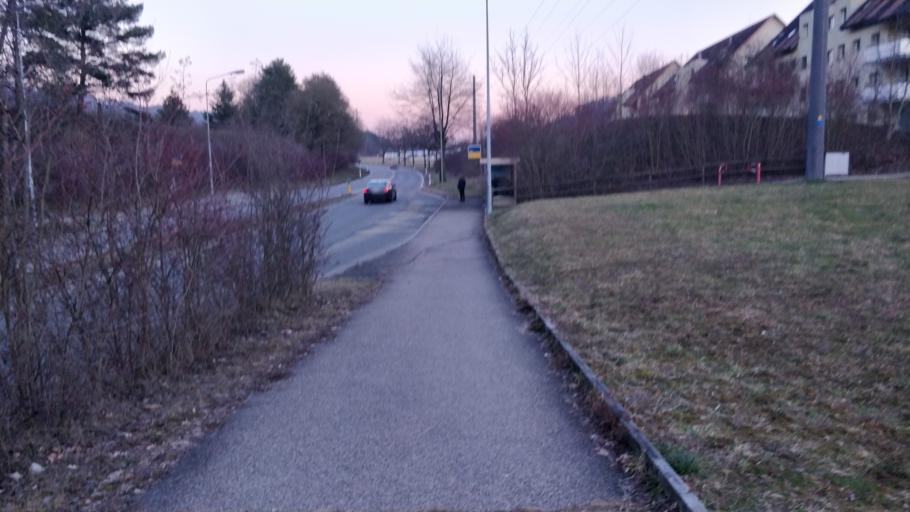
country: CH
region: Zurich
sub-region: Bezirk Buelach
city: Freienstein
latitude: 47.5226
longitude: 8.5848
